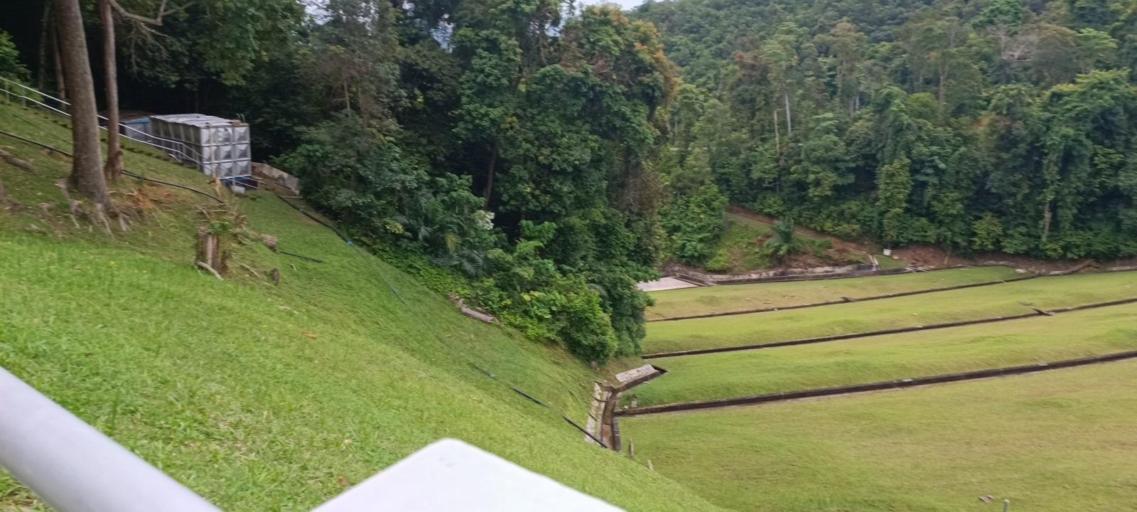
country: MY
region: Penang
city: Kampung Sungai Ara
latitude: 5.3971
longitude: 100.2633
